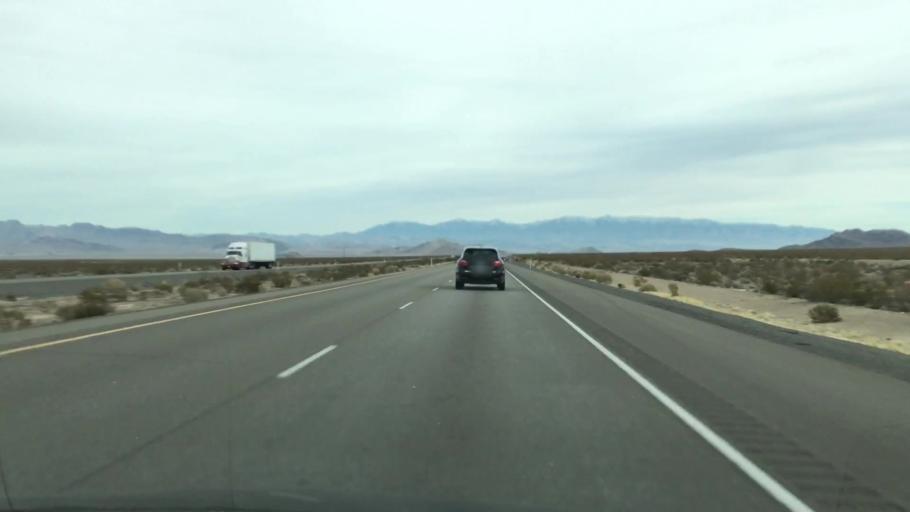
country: US
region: Nevada
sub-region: Nye County
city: Pahrump
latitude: 36.5733
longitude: -115.7633
